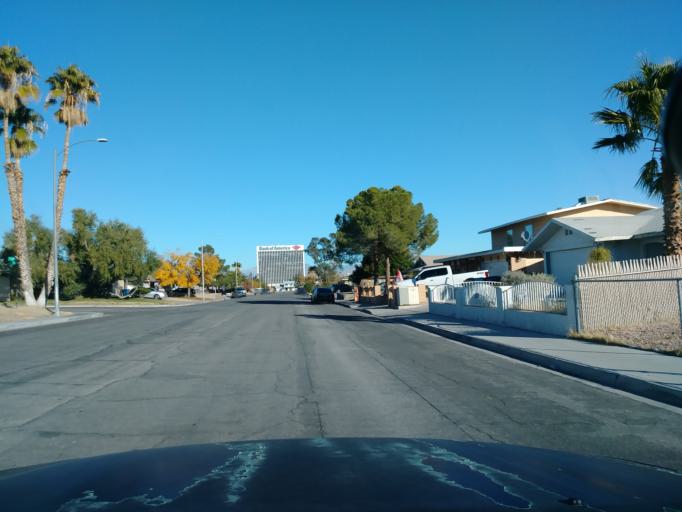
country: US
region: Nevada
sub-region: Clark County
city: Spring Valley
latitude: 36.1699
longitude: -115.2469
